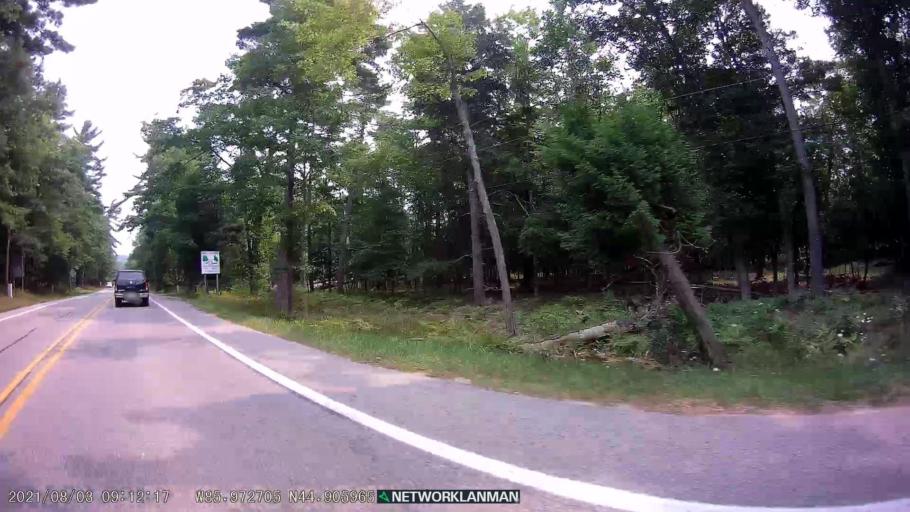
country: US
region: Michigan
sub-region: Leelanau County
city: Leland
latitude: 44.9062
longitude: -85.9726
